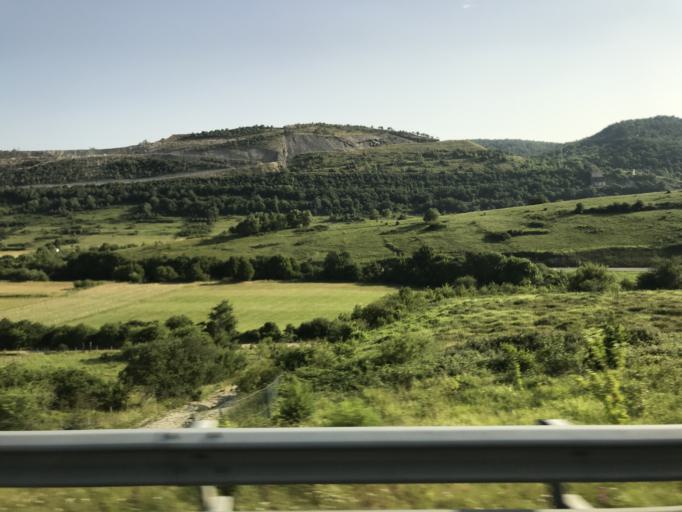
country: ES
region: Navarre
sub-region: Provincia de Navarra
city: Altsasu
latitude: 42.9155
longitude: -2.1880
